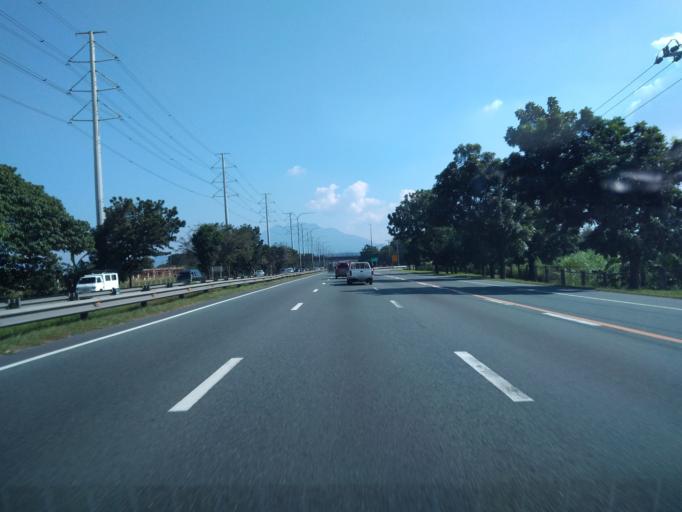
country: PH
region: Calabarzon
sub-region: Province of Laguna
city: Prinza
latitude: 14.2323
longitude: 121.1171
